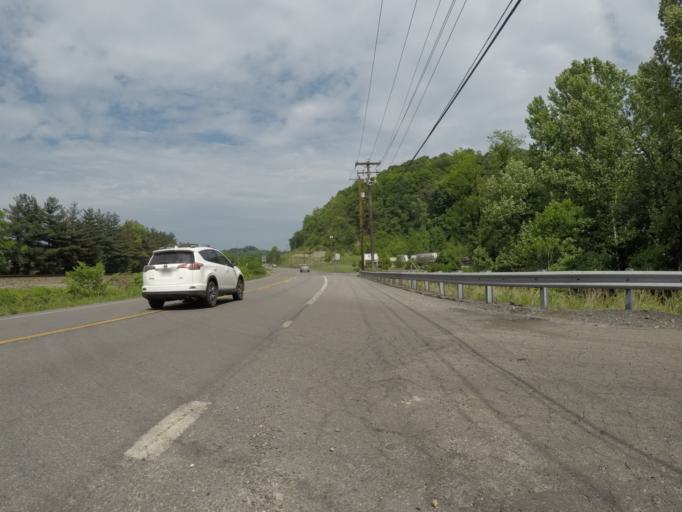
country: US
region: West Virginia
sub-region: Wayne County
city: Kenova
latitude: 38.3386
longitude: -82.5827
